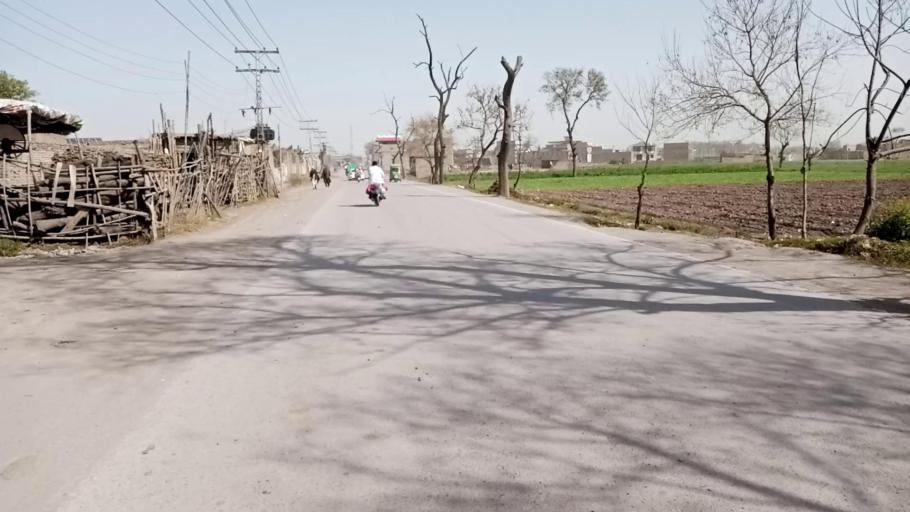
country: PK
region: Khyber Pakhtunkhwa
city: Peshawar
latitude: 33.9984
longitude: 71.6350
